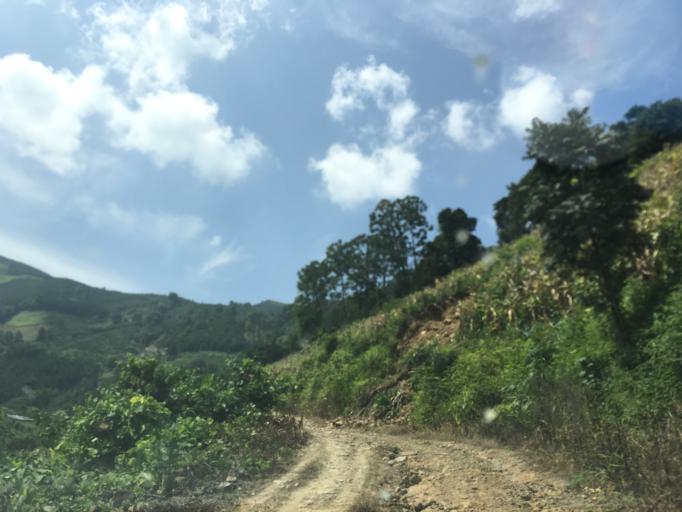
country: CN
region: Guangxi Zhuangzu Zizhiqu
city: Xinzhou
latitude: 24.9535
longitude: 105.7867
